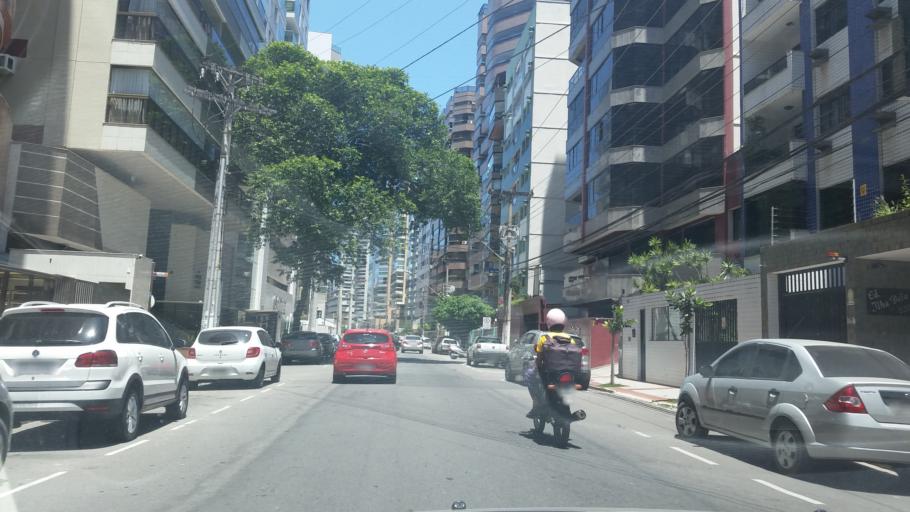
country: BR
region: Espirito Santo
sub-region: Vila Velha
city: Vila Velha
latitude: -20.3325
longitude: -40.2794
